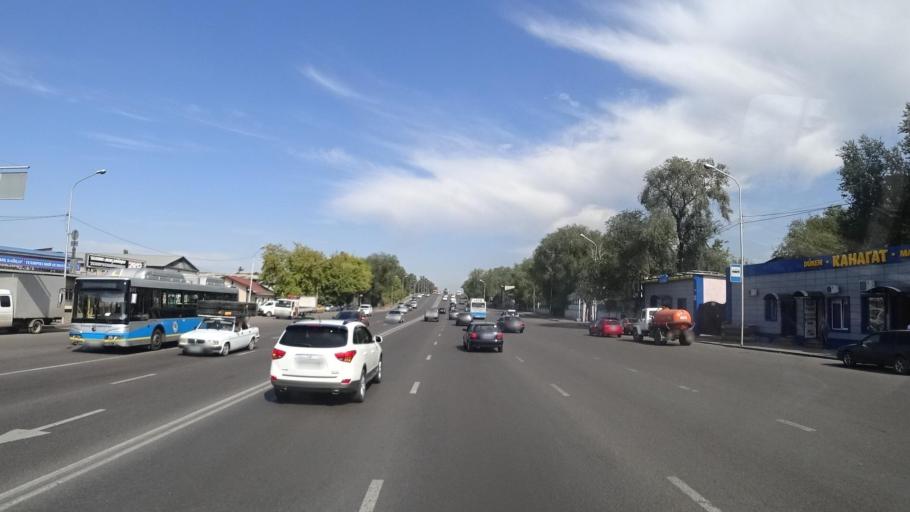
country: KZ
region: Almaty Qalasy
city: Almaty
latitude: 43.2792
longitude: 76.9061
